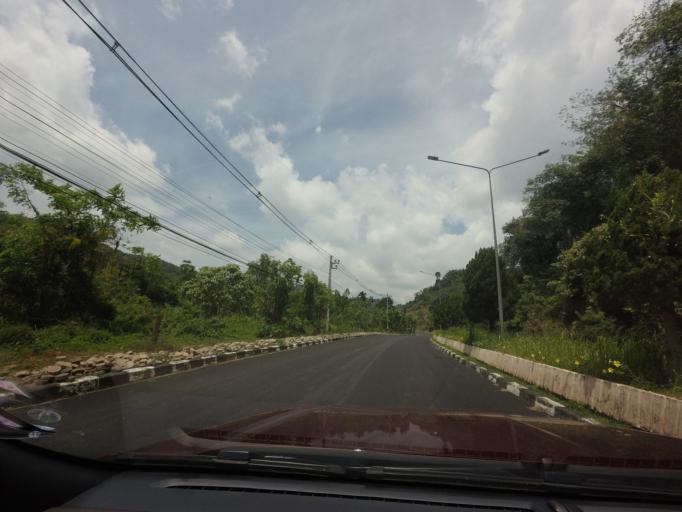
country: TH
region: Yala
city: Betong
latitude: 5.7579
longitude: 101.0449
